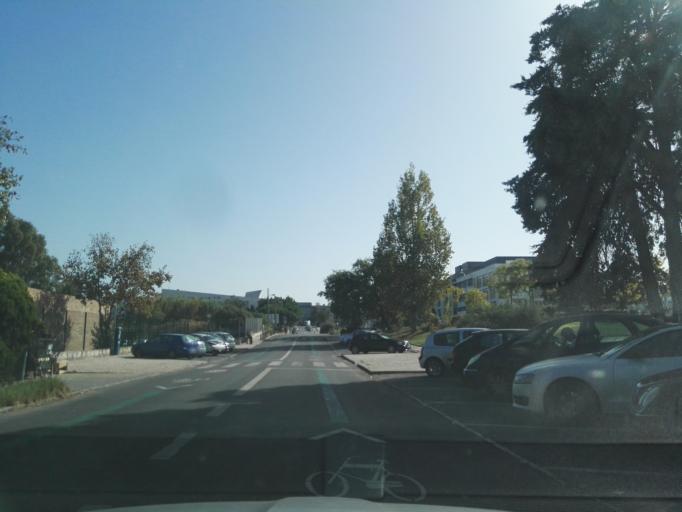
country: PT
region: Lisbon
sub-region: Odivelas
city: Olival do Basto
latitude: 38.7518
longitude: -9.1558
